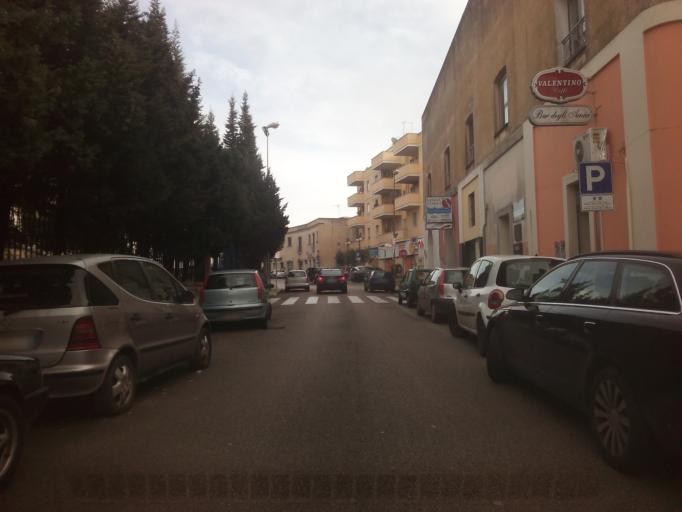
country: IT
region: Apulia
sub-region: Provincia di Lecce
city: Casarano
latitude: 40.0115
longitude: 18.1689
